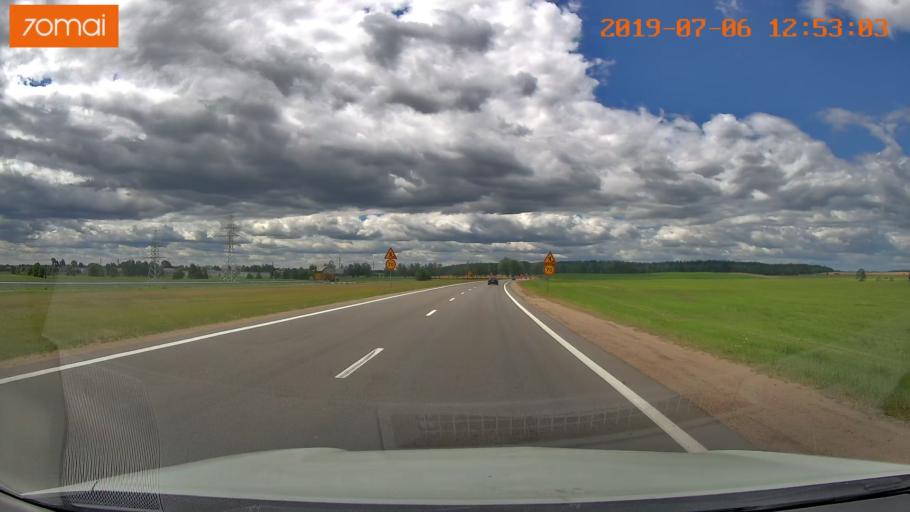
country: BY
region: Minsk
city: Dzyarzhynsk
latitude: 53.7046
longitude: 27.2095
